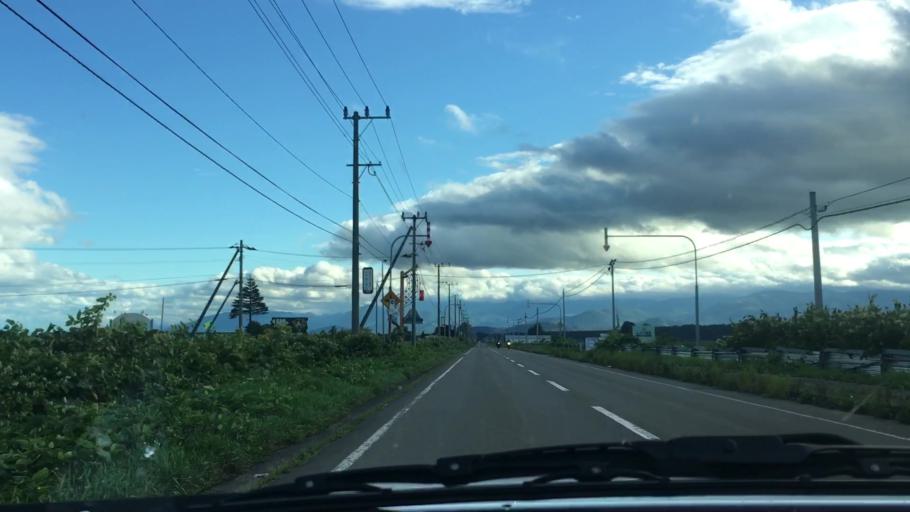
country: JP
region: Hokkaido
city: Otofuke
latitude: 43.1590
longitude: 142.9036
